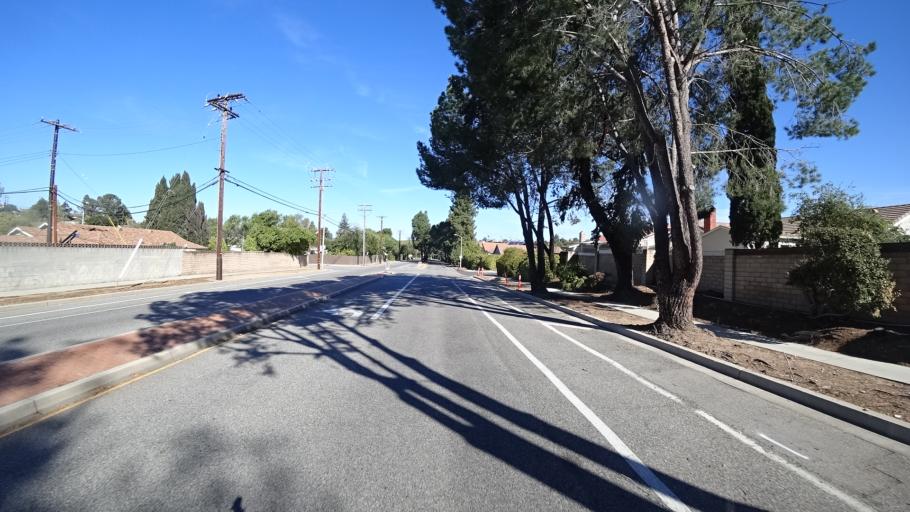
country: US
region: California
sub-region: Ventura County
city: Thousand Oaks
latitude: 34.2247
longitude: -118.8585
